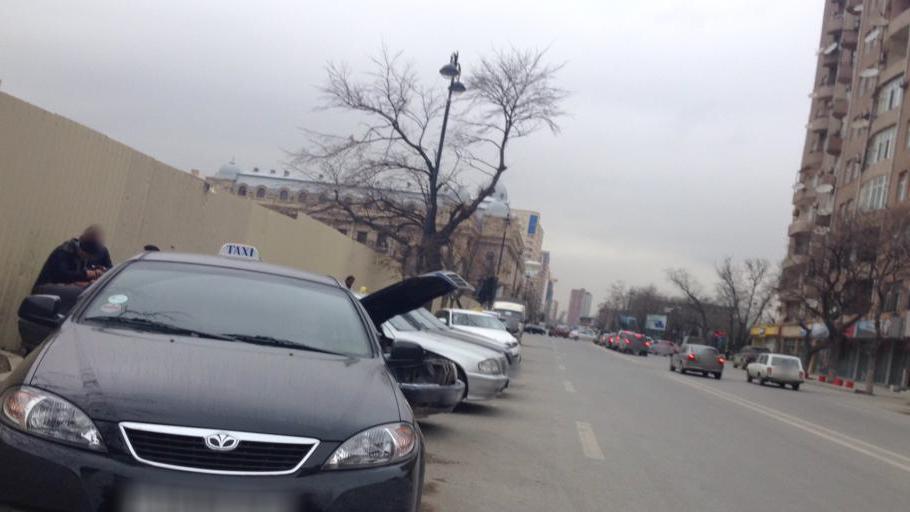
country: AZ
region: Baki
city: Baku
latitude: 40.3898
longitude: 49.8465
